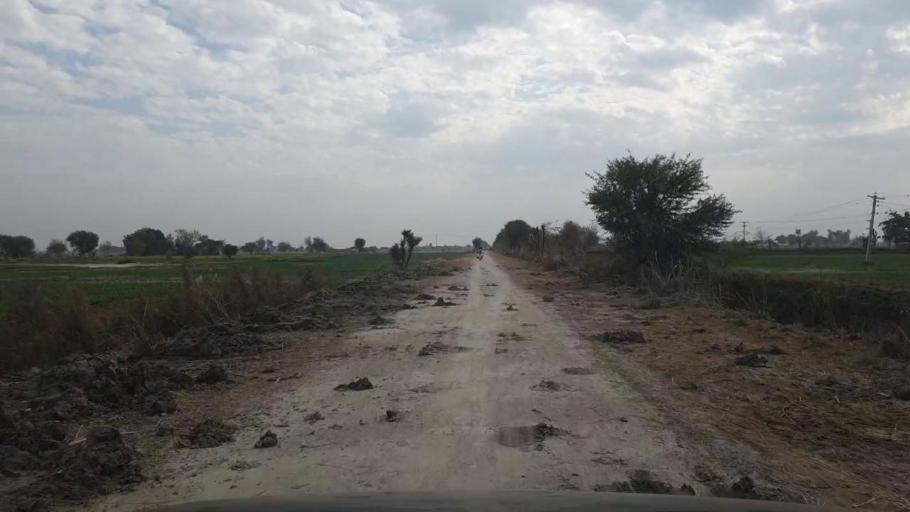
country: PK
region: Sindh
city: Sakrand
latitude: 26.0169
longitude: 68.4304
